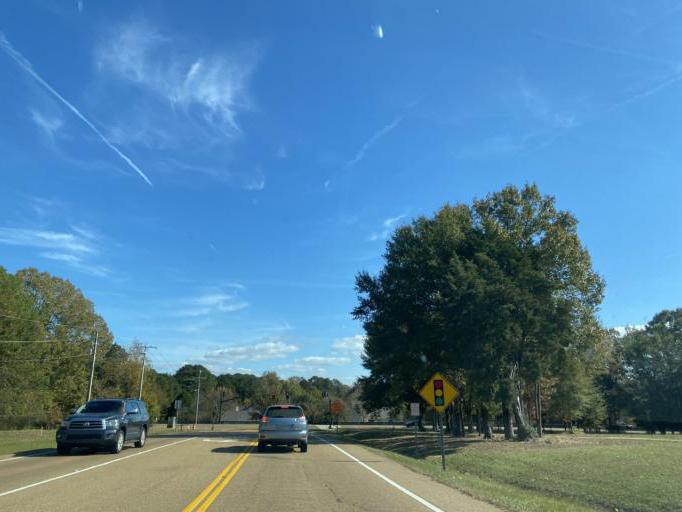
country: US
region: Mississippi
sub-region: Madison County
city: Madison
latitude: 32.4575
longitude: -90.0906
